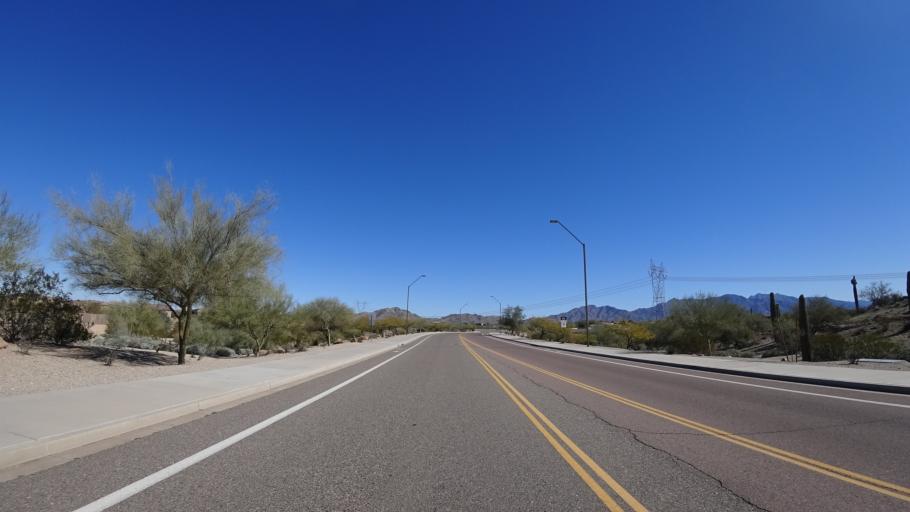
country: US
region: Arizona
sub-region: Maricopa County
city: Goodyear
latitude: 33.3236
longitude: -112.4415
